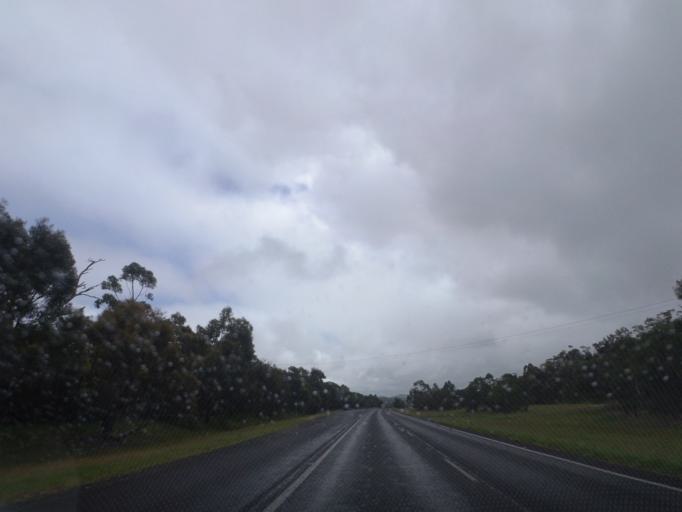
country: AU
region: Victoria
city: Black Hill
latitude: -37.5326
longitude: 143.8735
